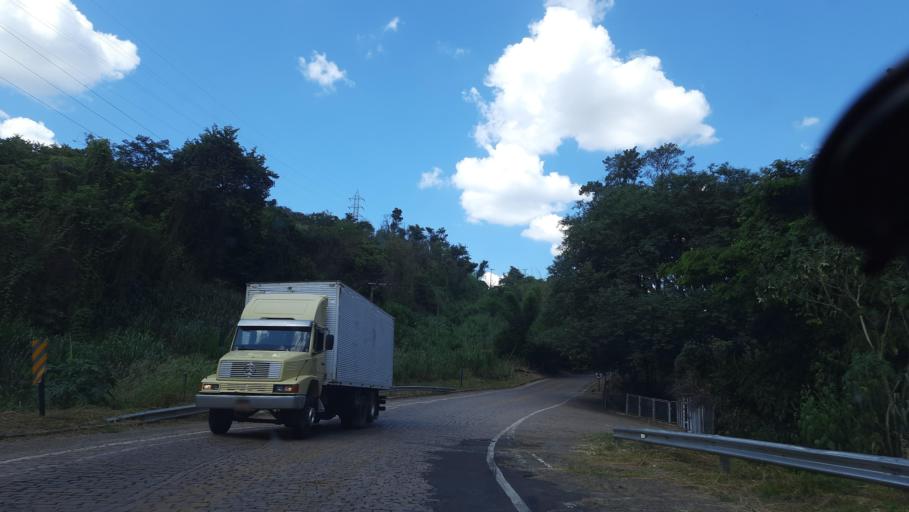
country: BR
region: Sao Paulo
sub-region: Sao Jose Do Rio Pardo
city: Sao Jose do Rio Pardo
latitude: -21.6033
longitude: -46.9556
